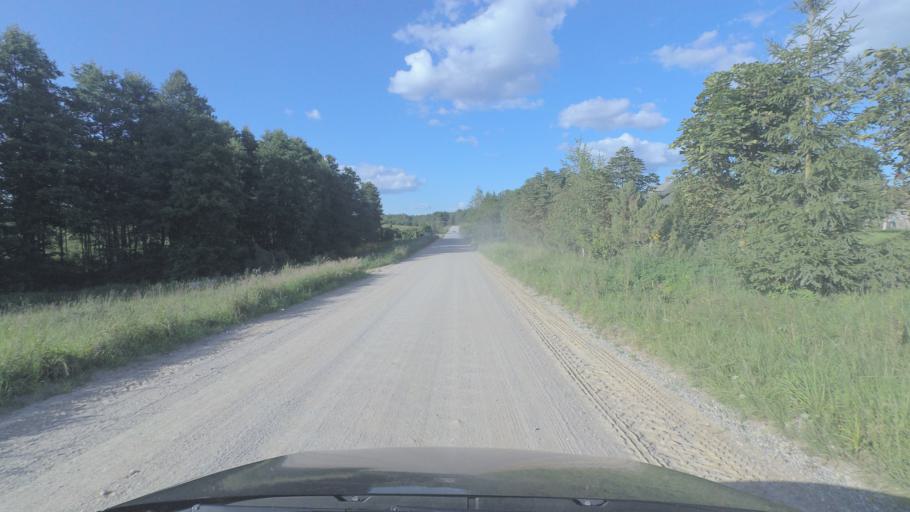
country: LT
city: Pabrade
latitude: 55.1369
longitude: 25.7098
